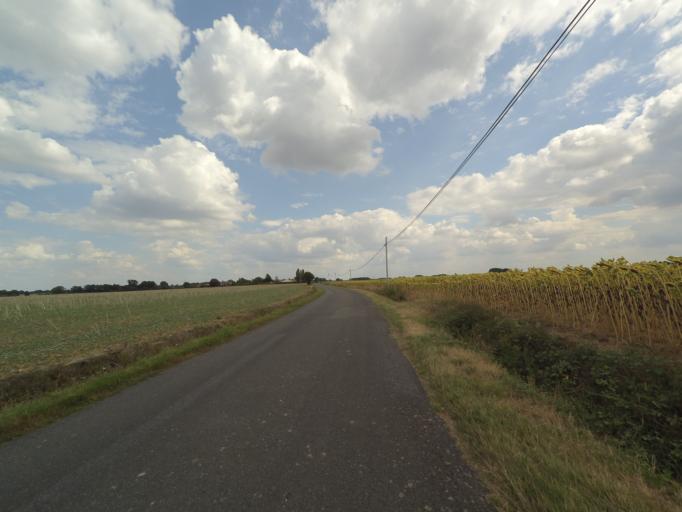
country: FR
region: Pays de la Loire
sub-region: Departement de la Loire-Atlantique
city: Vieillevigne
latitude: 46.9662
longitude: -1.4160
